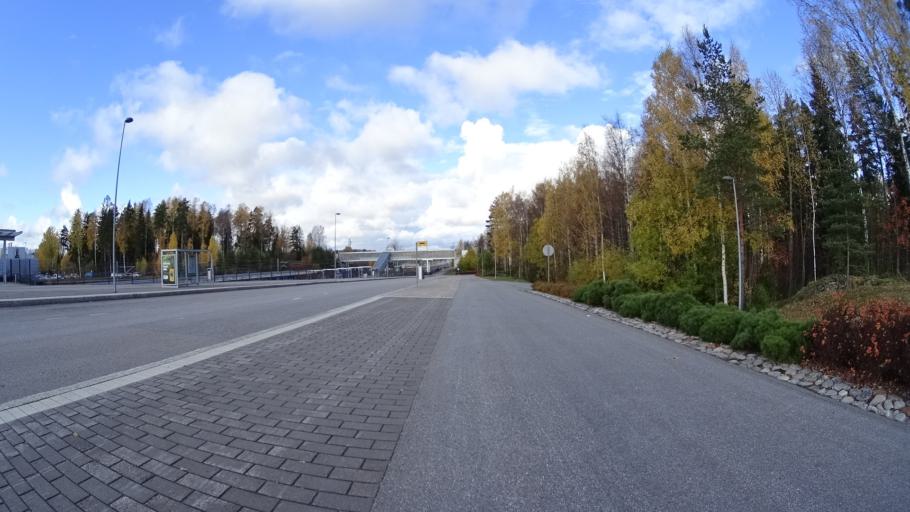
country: FI
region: Uusimaa
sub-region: Helsinki
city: Kilo
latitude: 60.2854
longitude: 24.8495
